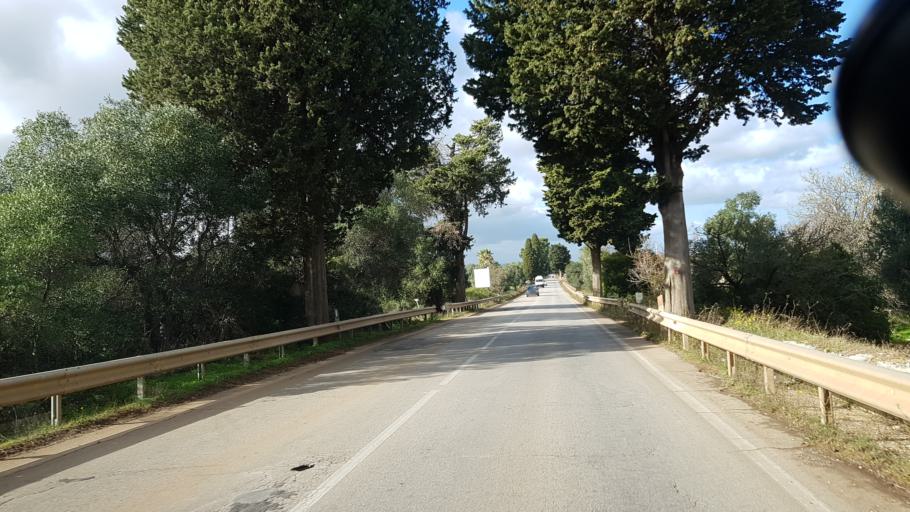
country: IT
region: Apulia
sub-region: Provincia di Brindisi
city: Ostuni
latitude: 40.7534
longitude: 17.5447
